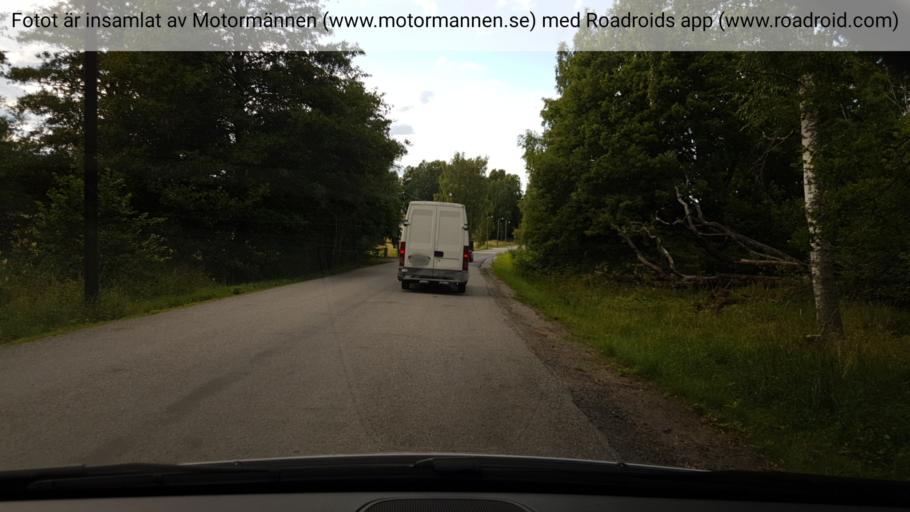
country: SE
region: Vaestmanland
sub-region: Vasteras
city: Vasteras
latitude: 59.5770
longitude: 16.6090
